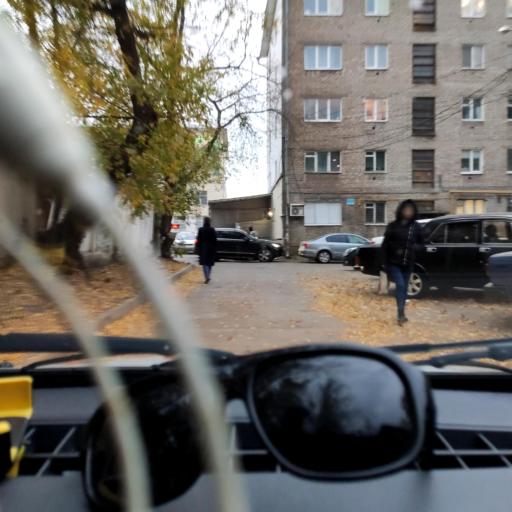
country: RU
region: Bashkortostan
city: Ufa
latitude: 54.7380
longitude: 55.9806
